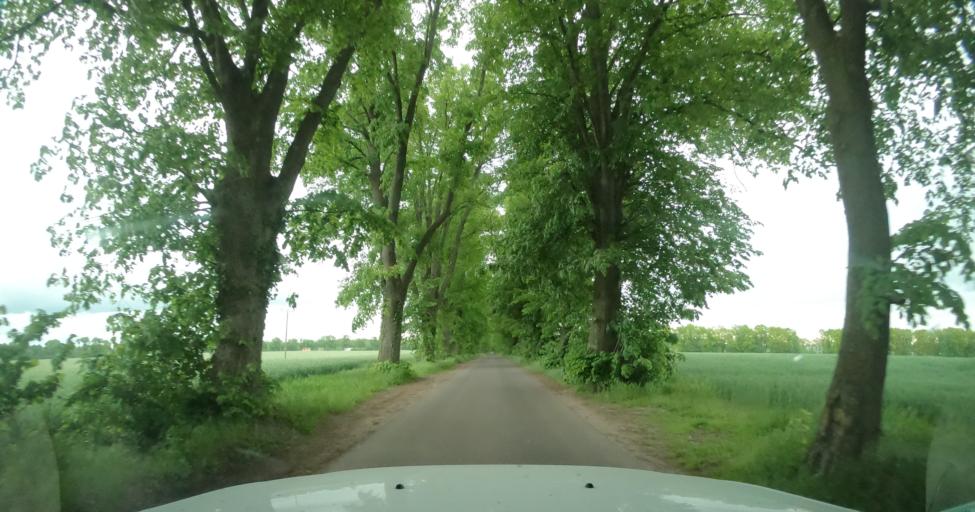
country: PL
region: West Pomeranian Voivodeship
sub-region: Powiat stargardzki
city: Dolice
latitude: 53.2456
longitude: 15.2499
